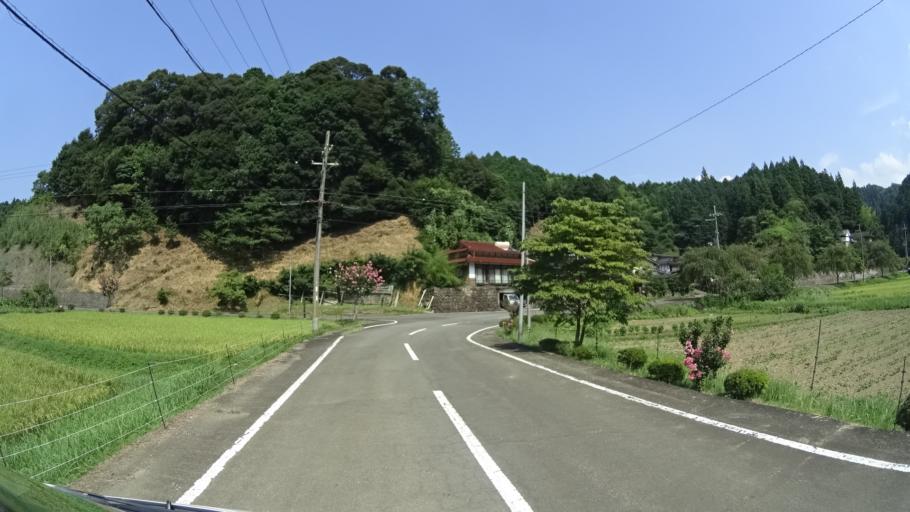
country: JP
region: Kyoto
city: Ayabe
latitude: 35.4050
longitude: 135.1985
